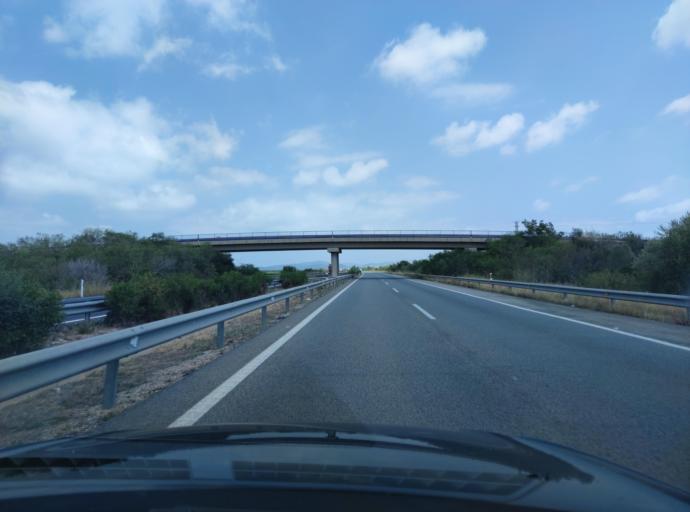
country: ES
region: Catalonia
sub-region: Provincia de Tarragona
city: Alcanar
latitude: 40.5244
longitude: 0.4171
